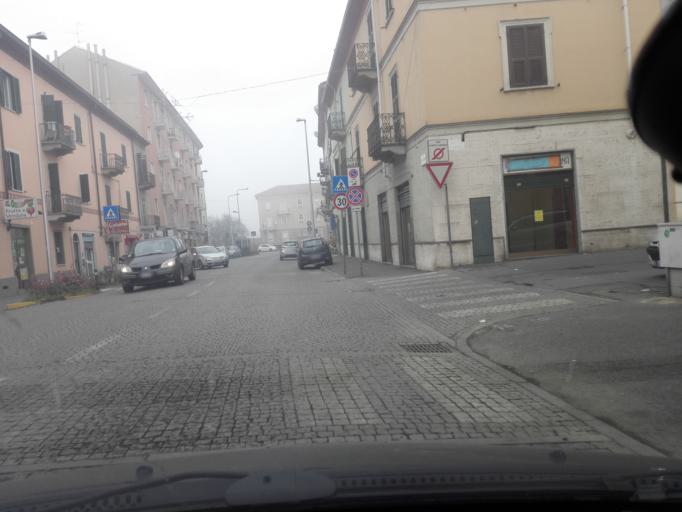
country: IT
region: Piedmont
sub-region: Provincia di Alessandria
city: Alessandria
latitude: 44.9034
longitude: 8.6039
